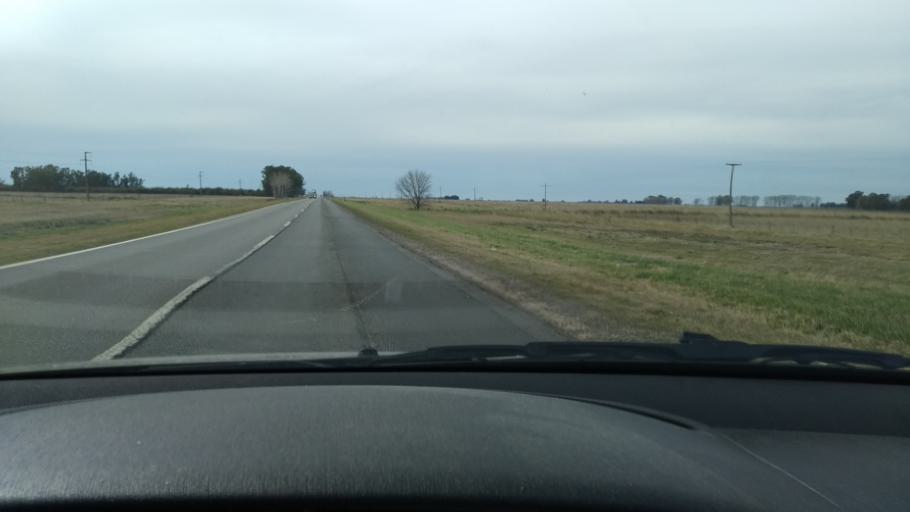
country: AR
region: Buenos Aires
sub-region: Partido de Azul
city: Azul
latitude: -36.7486
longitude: -59.8006
